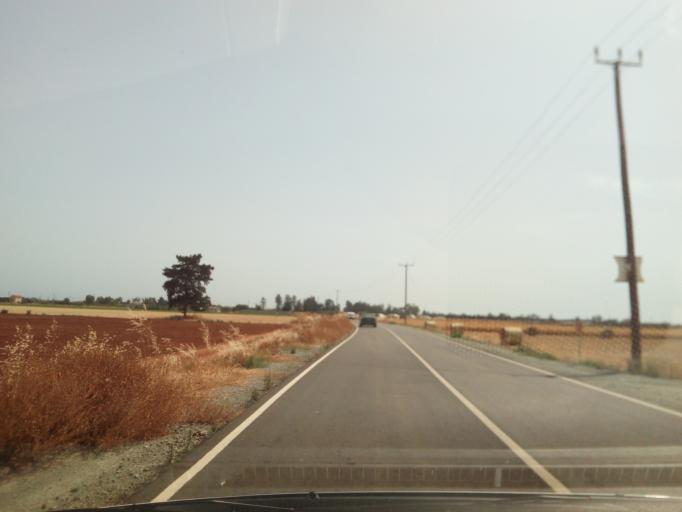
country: CY
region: Larnaka
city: Perivolia
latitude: 34.8443
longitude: 33.5930
